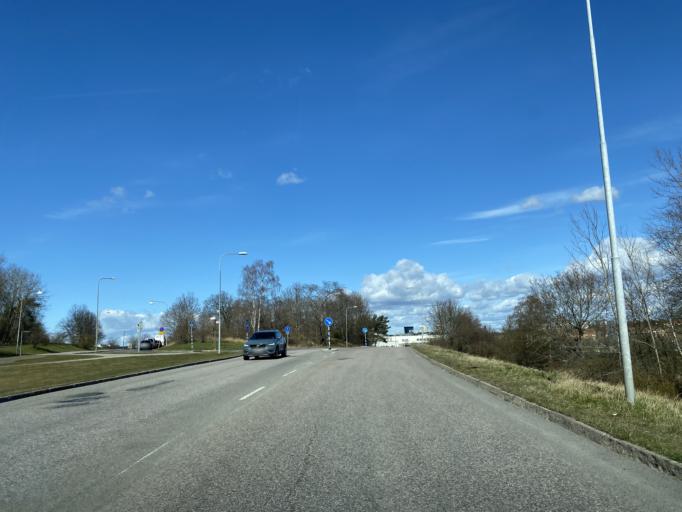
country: SE
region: Stockholm
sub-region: Stockholms Kommun
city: Arsta
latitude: 59.2901
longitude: 18.0375
